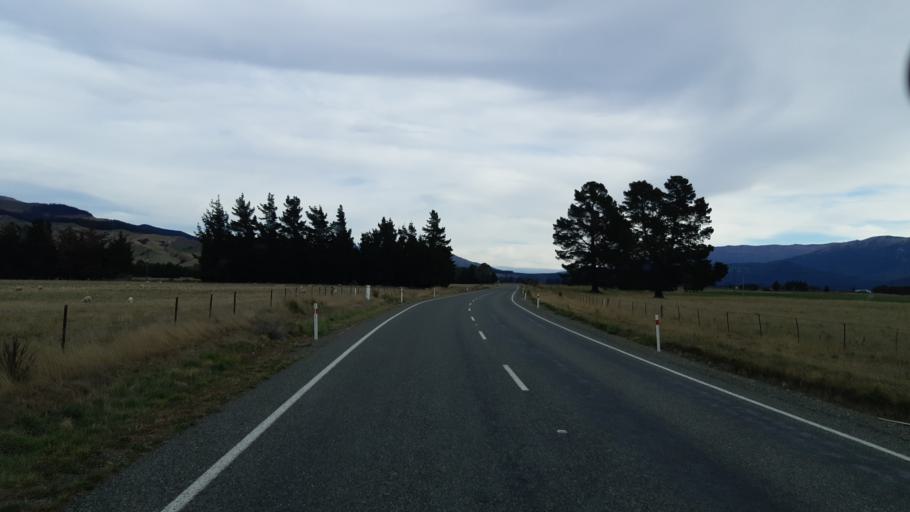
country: NZ
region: Tasman
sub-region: Tasman District
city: Brightwater
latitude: -41.6405
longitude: 173.3091
